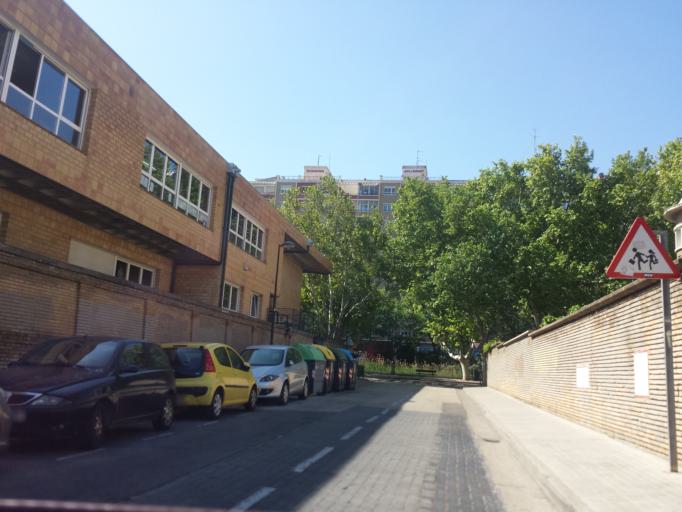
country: ES
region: Aragon
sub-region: Provincia de Zaragoza
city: Zaragoza
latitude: 41.6342
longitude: -0.8872
